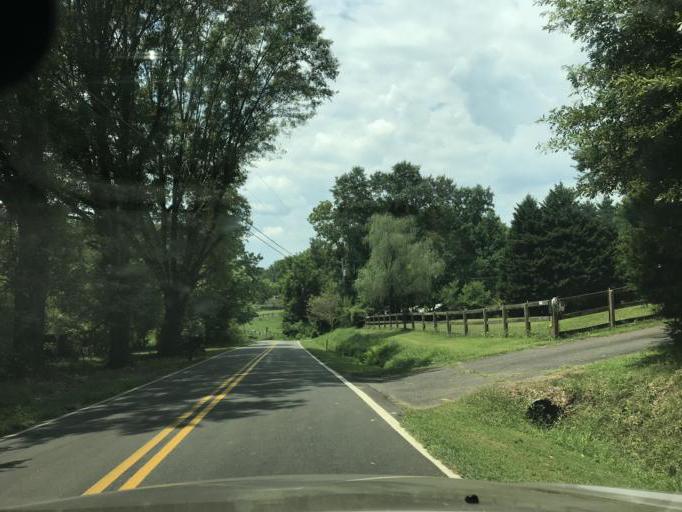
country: US
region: Georgia
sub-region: Dawson County
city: Dawsonville
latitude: 34.3315
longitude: -84.1971
